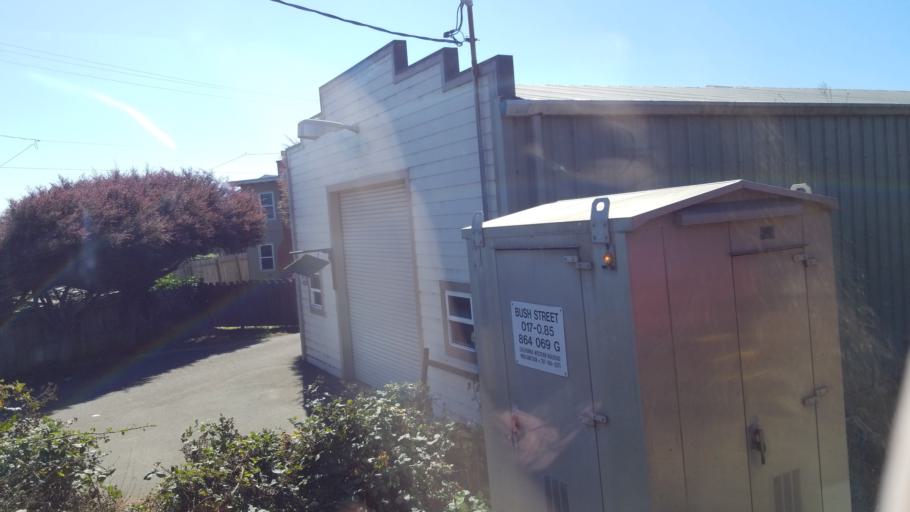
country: US
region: California
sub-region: Mendocino County
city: Fort Bragg
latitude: 39.4491
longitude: -123.8042
